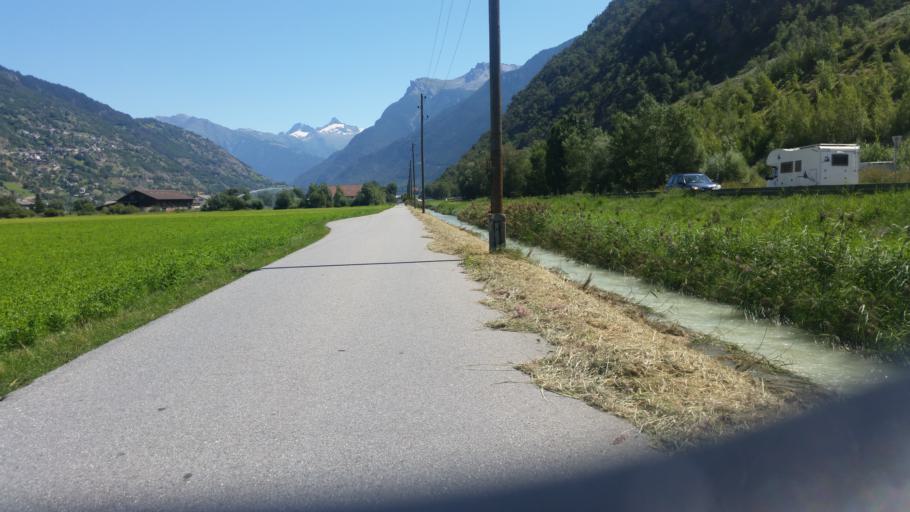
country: CH
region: Valais
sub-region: Visp District
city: Baltschieder
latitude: 46.2987
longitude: 7.8440
